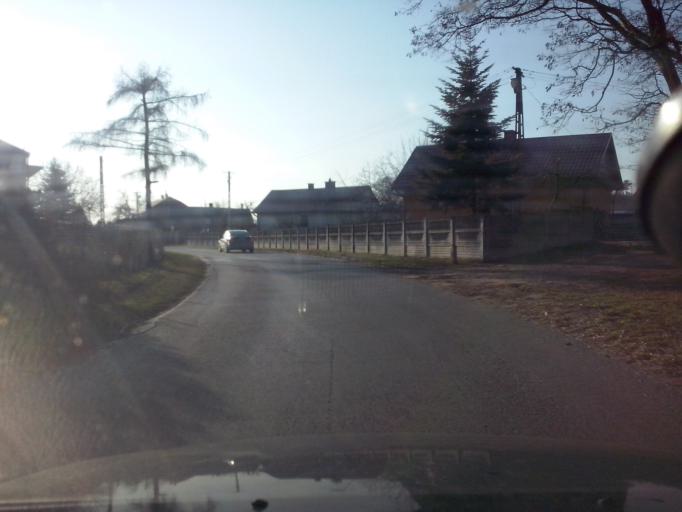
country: PL
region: Subcarpathian Voivodeship
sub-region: Powiat lezajski
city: Letownia
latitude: 50.3430
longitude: 22.1996
